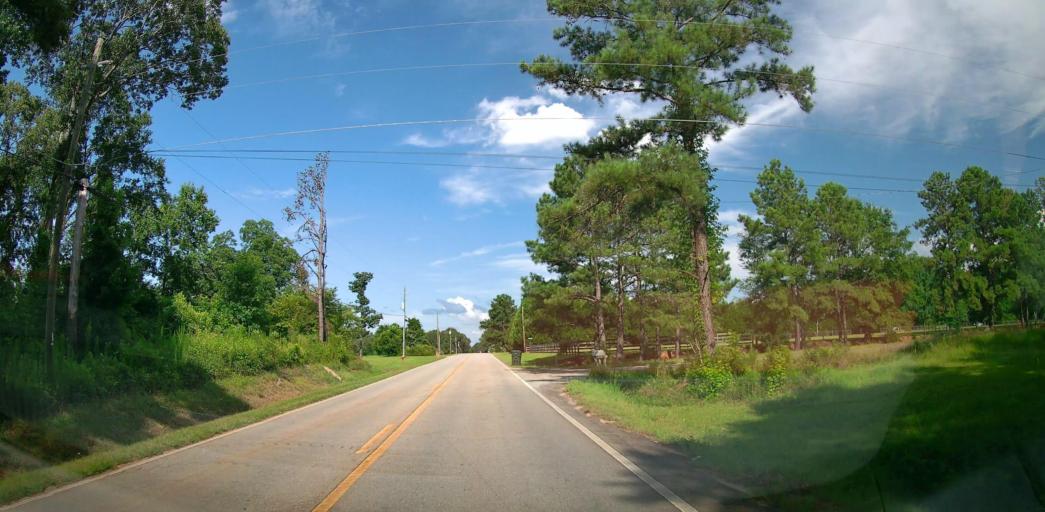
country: US
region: Georgia
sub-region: Houston County
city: Robins Air Force Base
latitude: 32.5382
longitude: -83.6496
